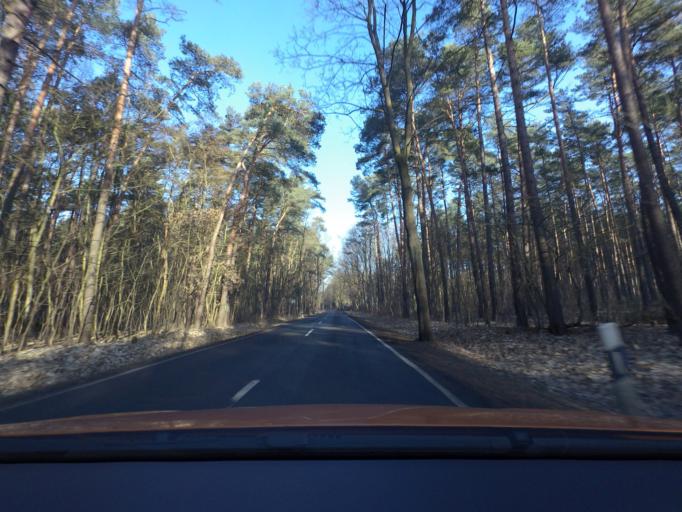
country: DE
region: Brandenburg
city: Wandlitz
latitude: 52.7417
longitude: 13.3713
